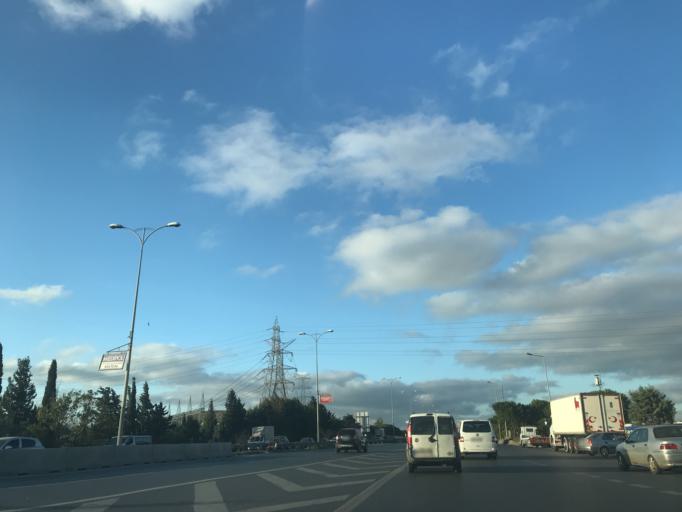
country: TR
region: Istanbul
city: Esenler
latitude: 41.0499
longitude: 28.8855
